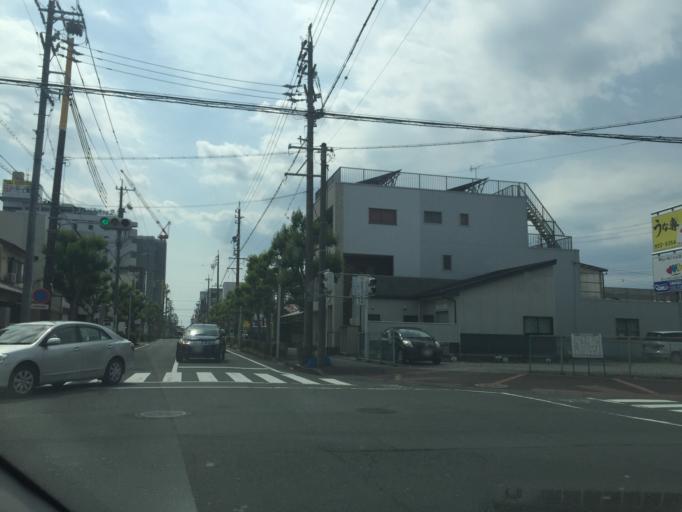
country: JP
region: Shizuoka
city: Kakegawa
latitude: 34.7716
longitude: 138.0187
